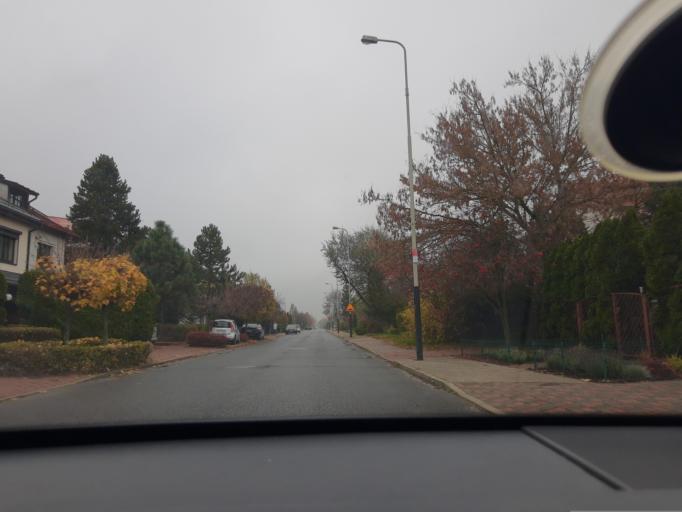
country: PL
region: Lodz Voivodeship
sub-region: Powiat pabianicki
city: Konstantynow Lodzki
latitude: 51.7402
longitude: 19.3793
